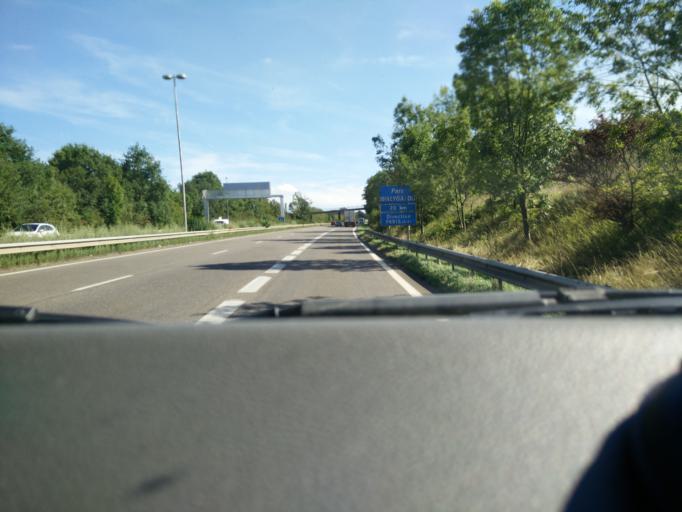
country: FR
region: Lorraine
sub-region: Departement de la Moselle
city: Illange
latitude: 49.3421
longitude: 6.1808
